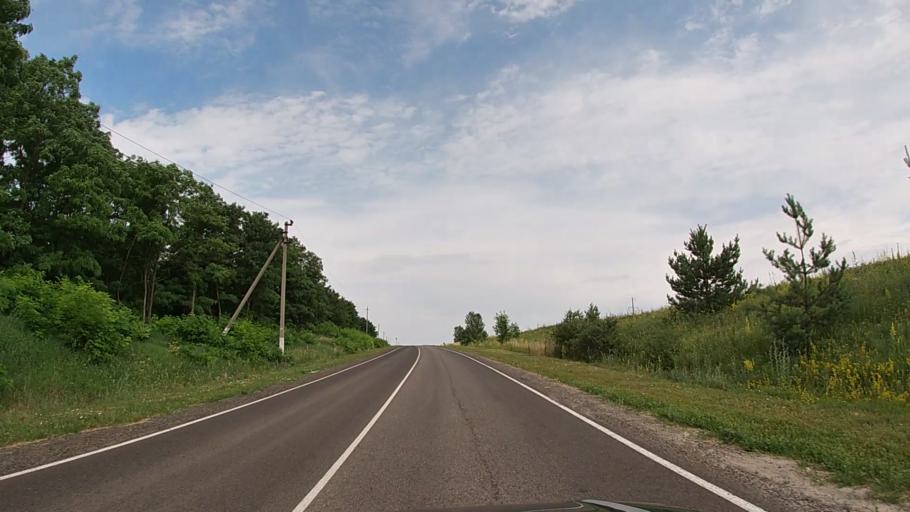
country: RU
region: Belgorod
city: Krasnaya Yaruga
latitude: 50.8304
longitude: 35.4946
